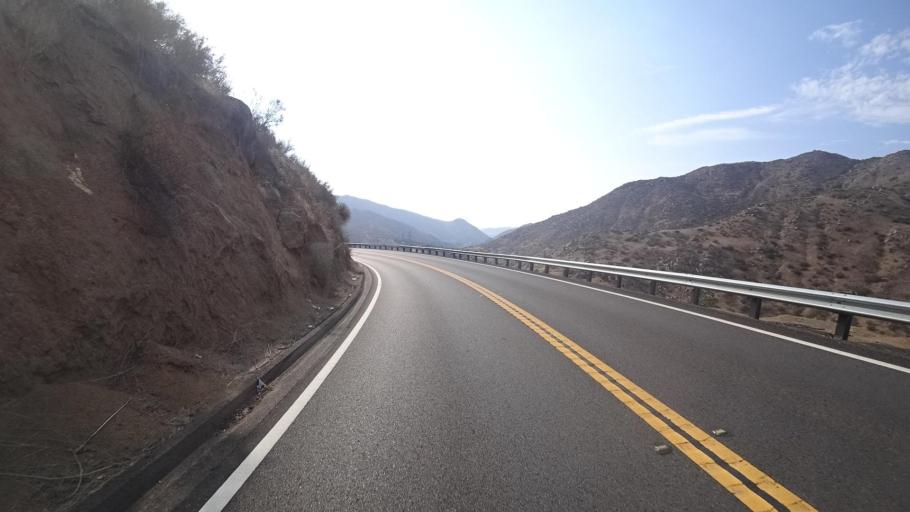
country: US
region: California
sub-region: San Diego County
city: San Pasqual
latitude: 33.0871
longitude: -116.9088
